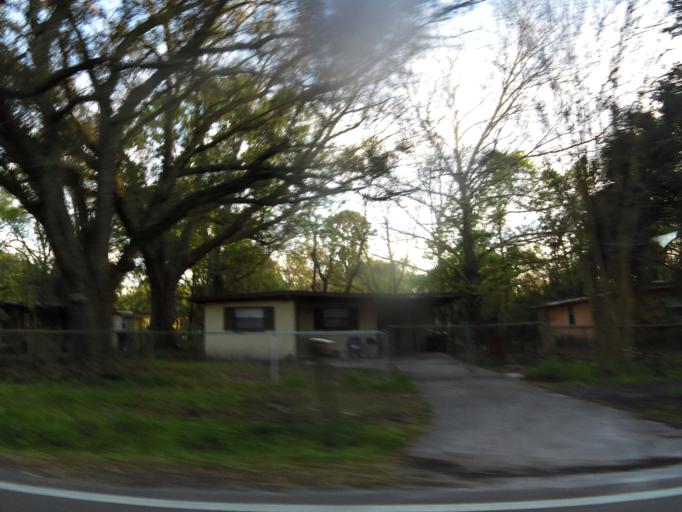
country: US
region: Florida
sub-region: Duval County
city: Jacksonville
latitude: 30.3402
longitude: -81.7195
